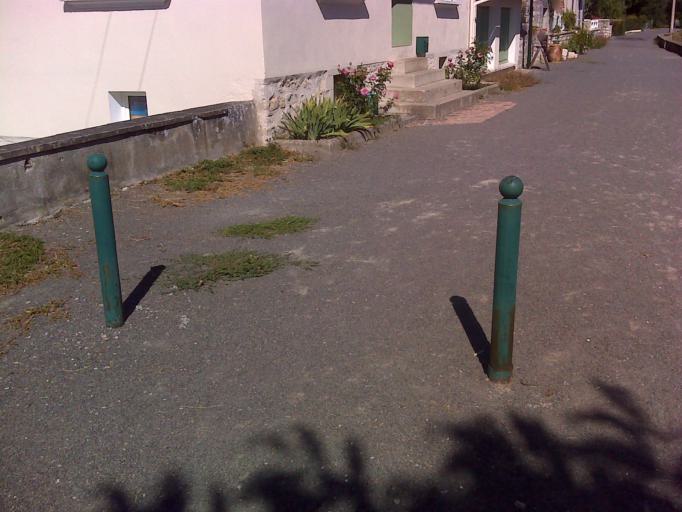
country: FR
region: Auvergne
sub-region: Departement de l'Allier
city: Ebreuil
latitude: 46.1159
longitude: 3.0920
